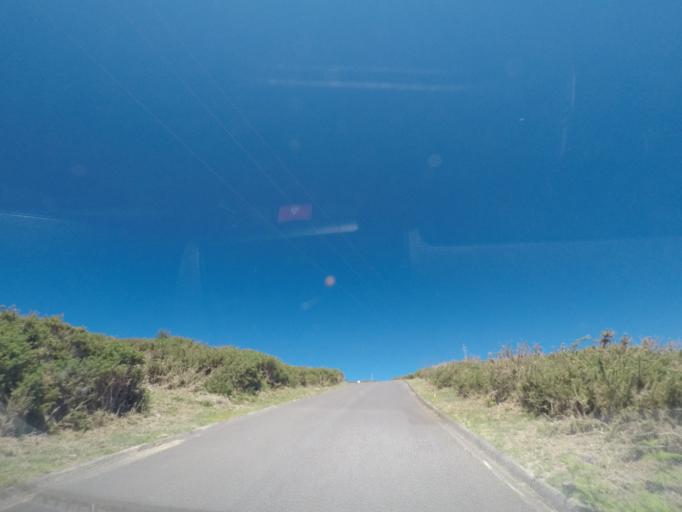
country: PT
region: Madeira
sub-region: Calheta
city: Arco da Calheta
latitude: 32.7479
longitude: -17.1260
